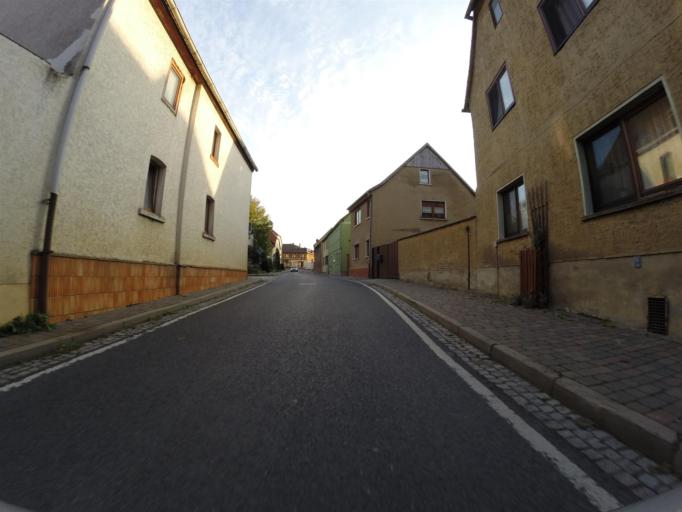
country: DE
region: Thuringia
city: Magdala
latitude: 50.9079
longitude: 11.4489
